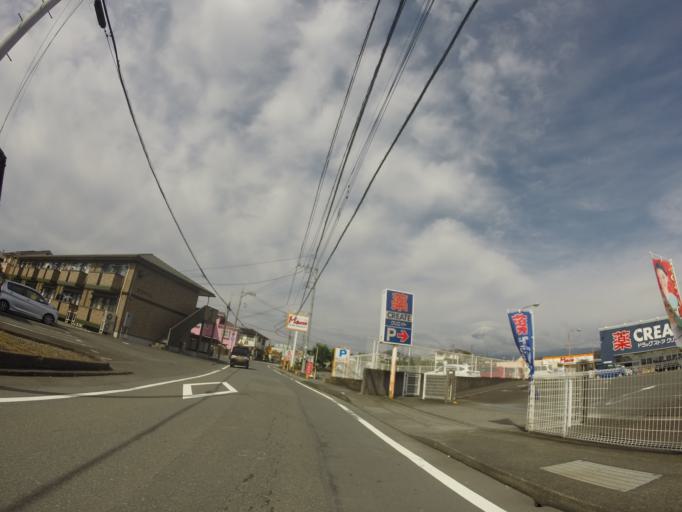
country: JP
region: Shizuoka
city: Fuji
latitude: 35.1808
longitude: 138.6917
